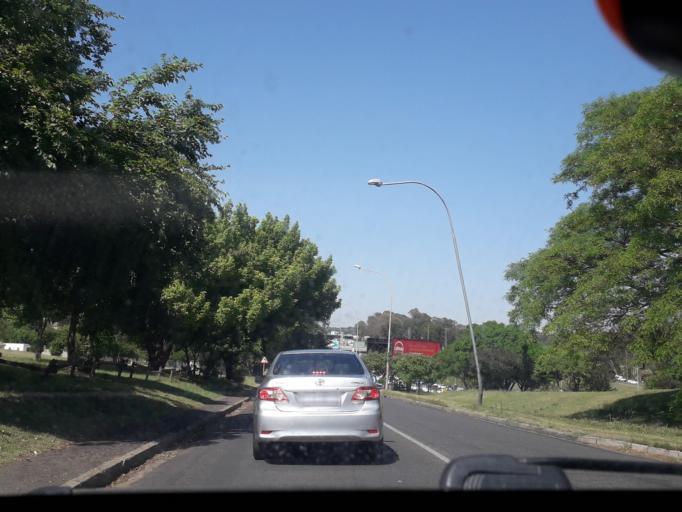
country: ZA
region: Gauteng
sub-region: City of Johannesburg Metropolitan Municipality
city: Johannesburg
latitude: -26.1369
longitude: 28.0704
